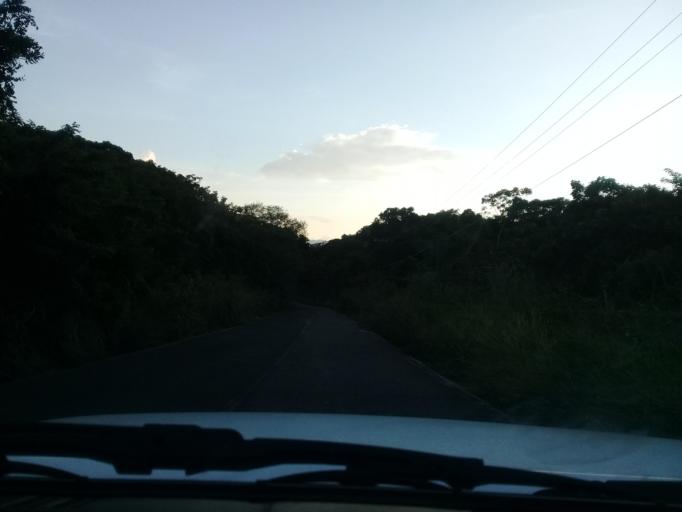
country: MX
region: Veracruz
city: Catemaco
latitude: 18.4357
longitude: -95.0900
